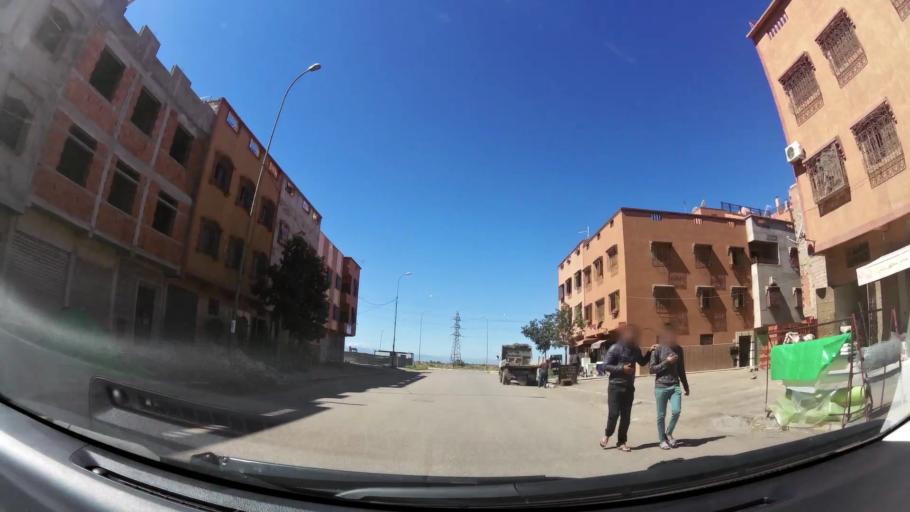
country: MA
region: Marrakech-Tensift-Al Haouz
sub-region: Marrakech
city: Marrakesh
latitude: 31.5712
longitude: -8.0578
